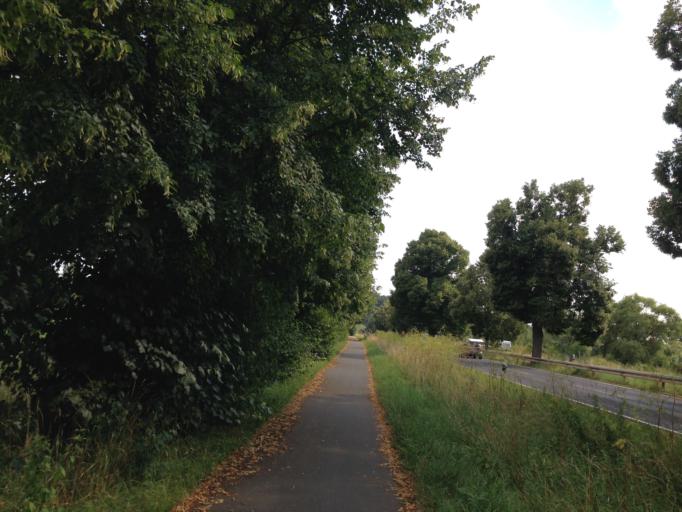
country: DE
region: Hesse
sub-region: Regierungsbezirk Giessen
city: Heuchelheim
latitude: 50.5693
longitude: 8.6293
